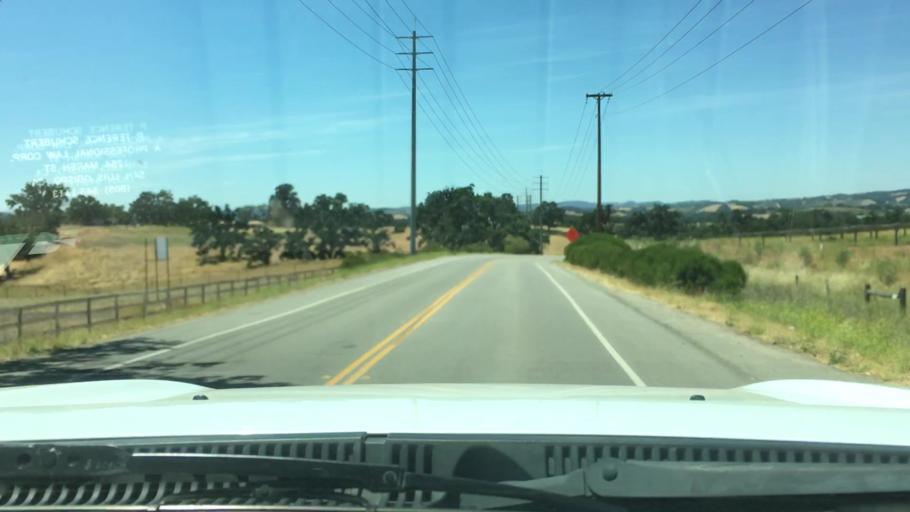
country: US
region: California
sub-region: San Luis Obispo County
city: Templeton
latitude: 35.5570
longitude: -120.6831
